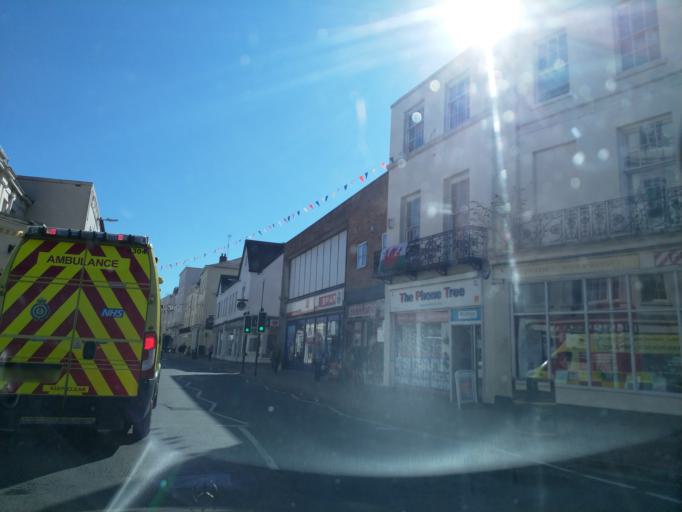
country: GB
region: England
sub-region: Warwickshire
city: Royal Leamington Spa
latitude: 52.2858
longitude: -1.5330
